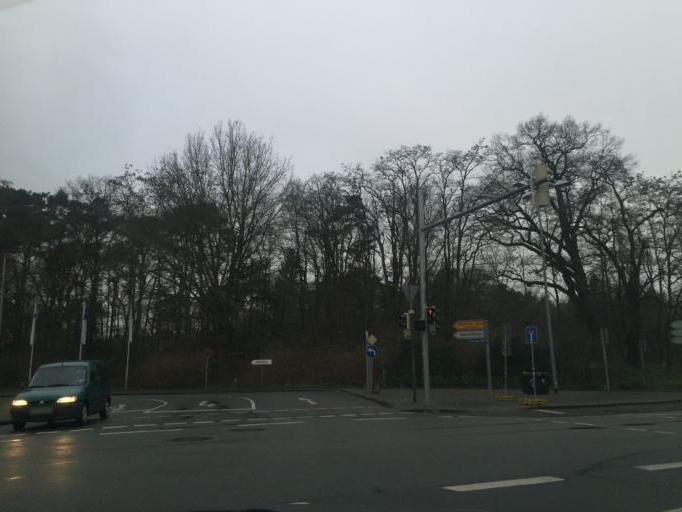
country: DE
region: Lower Saxony
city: Celle
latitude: 52.6180
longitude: 10.0516
